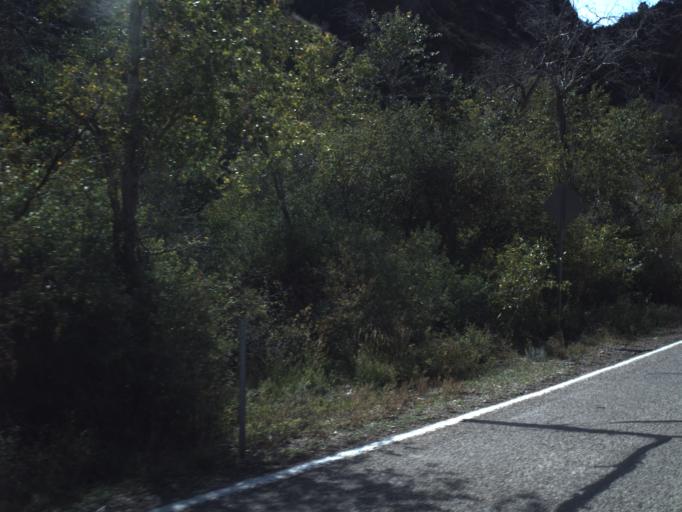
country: US
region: Utah
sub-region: Beaver County
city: Beaver
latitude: 38.2797
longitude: -112.5679
